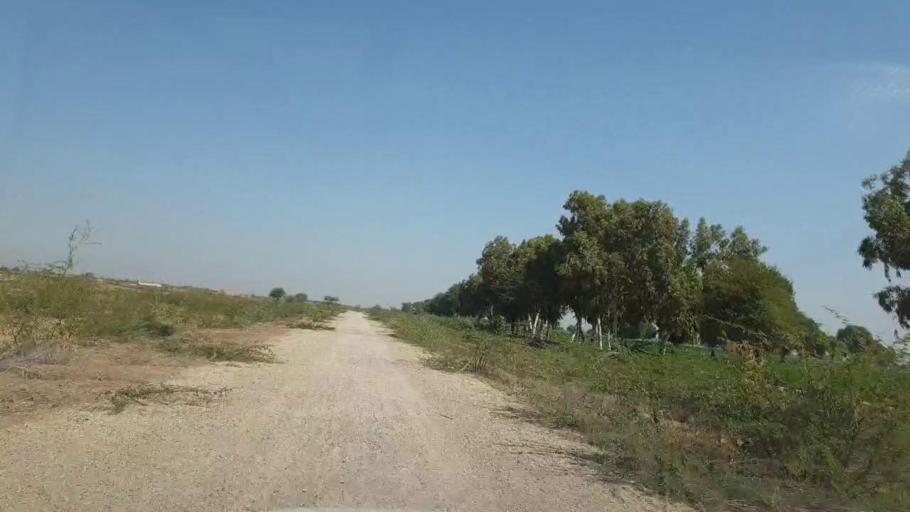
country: PK
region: Sindh
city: Kunri
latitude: 25.1371
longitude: 69.5099
